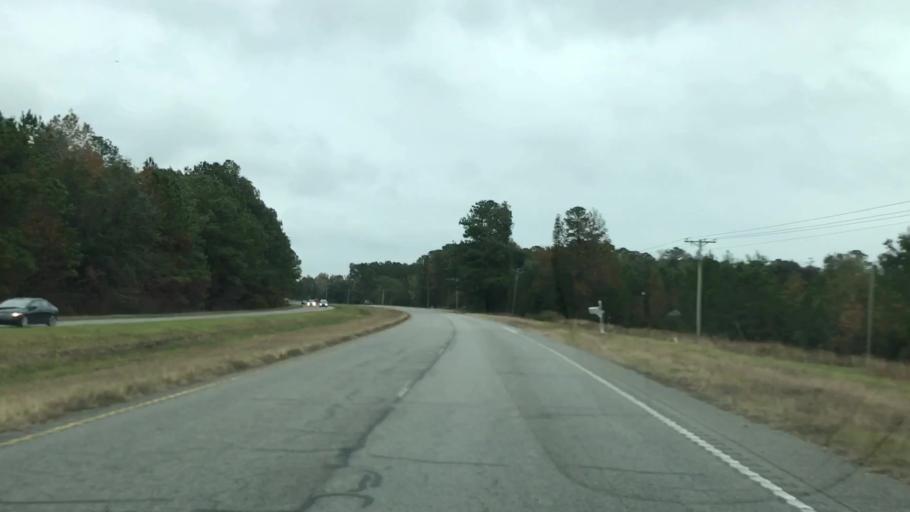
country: US
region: South Carolina
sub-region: Charleston County
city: Awendaw
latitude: 33.0394
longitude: -79.5940
